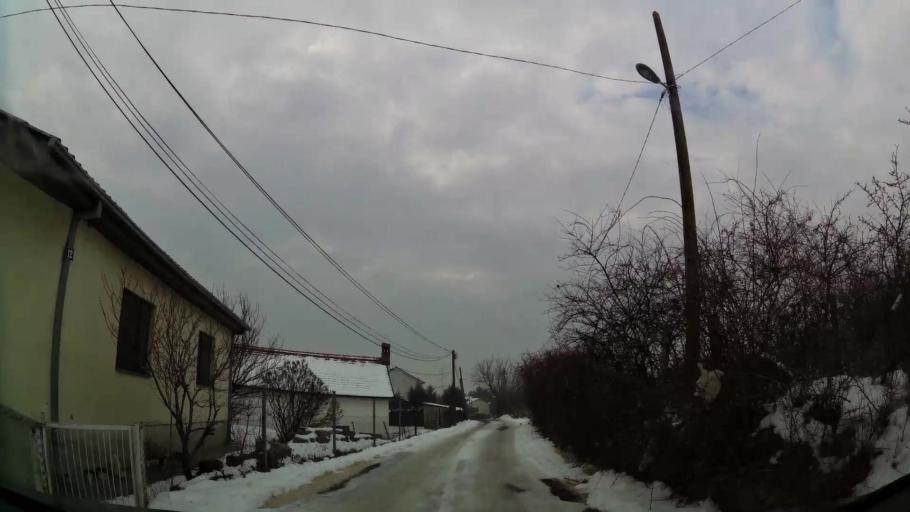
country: MK
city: Kondovo
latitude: 42.0379
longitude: 21.3439
